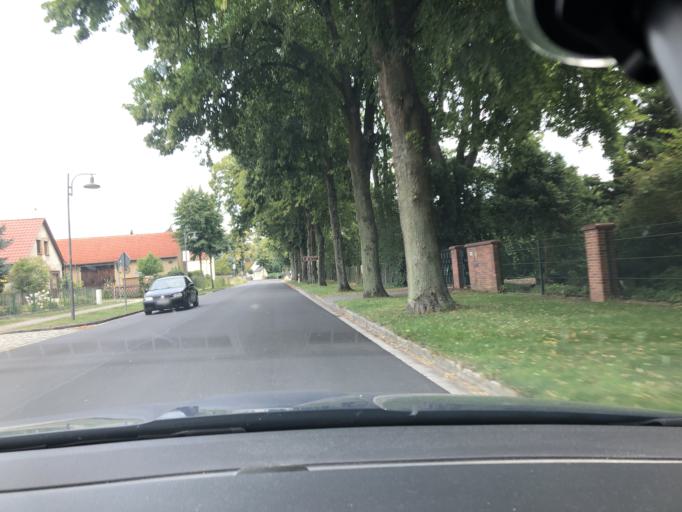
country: DE
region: Brandenburg
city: Schlepzig
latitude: 52.0324
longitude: 13.8329
